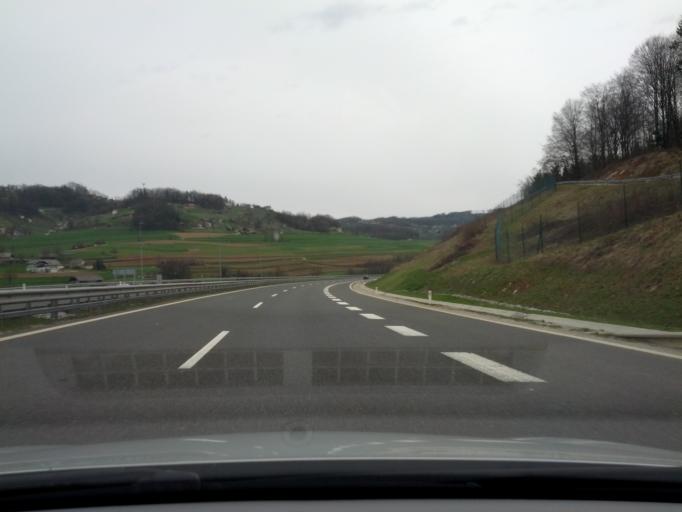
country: SI
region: Mirna Pec
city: Mirna Pec
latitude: 45.8736
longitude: 15.1010
